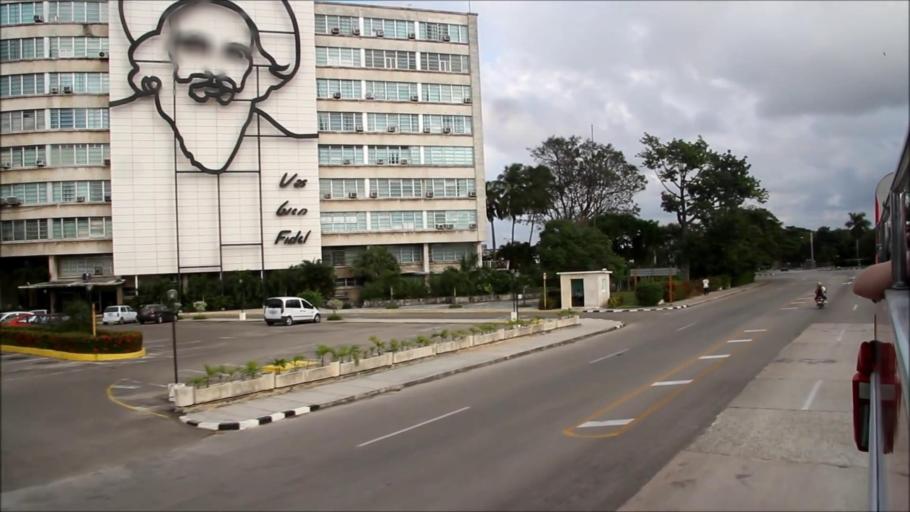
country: CU
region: La Habana
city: Havana
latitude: 23.1248
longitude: -82.3852
